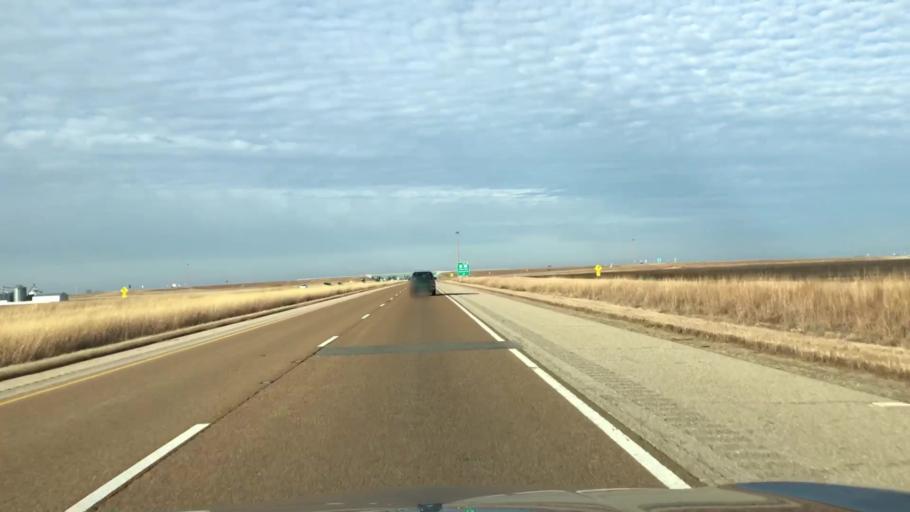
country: US
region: Illinois
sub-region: Montgomery County
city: Raymond
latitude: 39.3140
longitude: -89.6423
